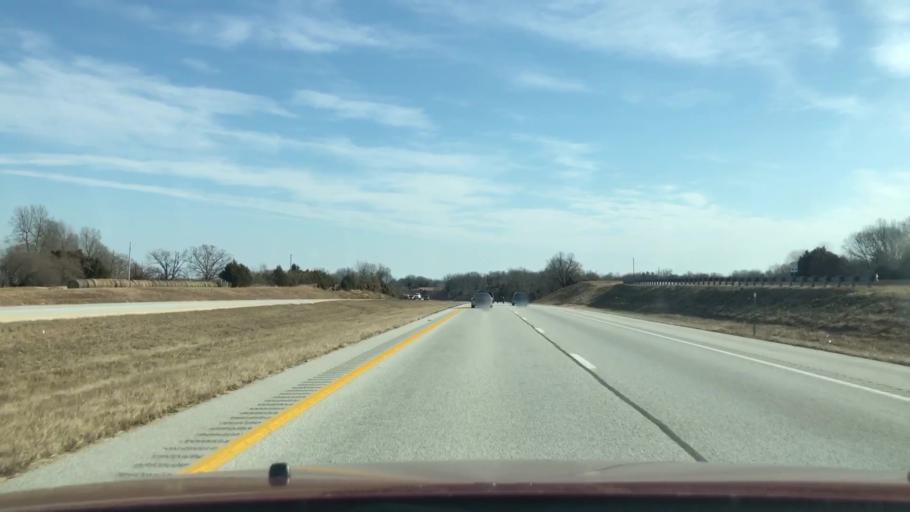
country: US
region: Missouri
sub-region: Webster County
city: Seymour
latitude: 37.1604
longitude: -92.9003
